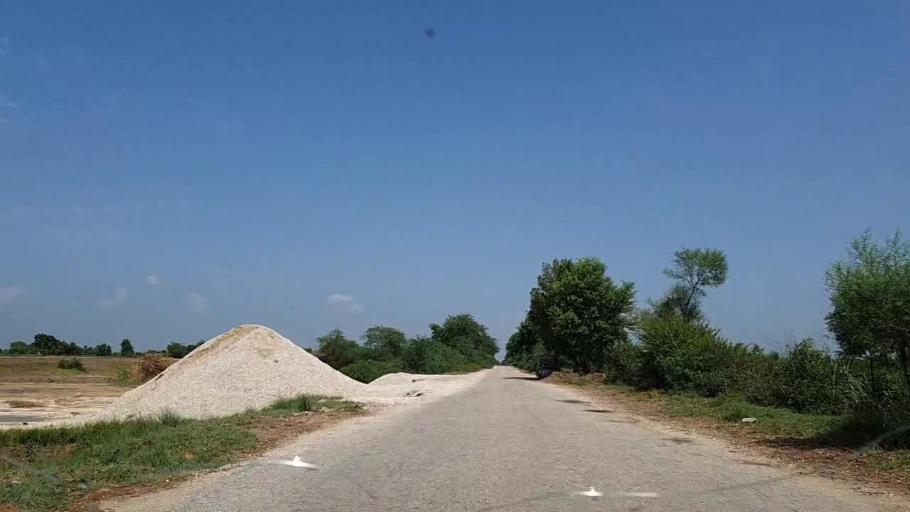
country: PK
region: Sindh
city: Naushahro Firoz
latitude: 26.8070
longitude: 68.2075
